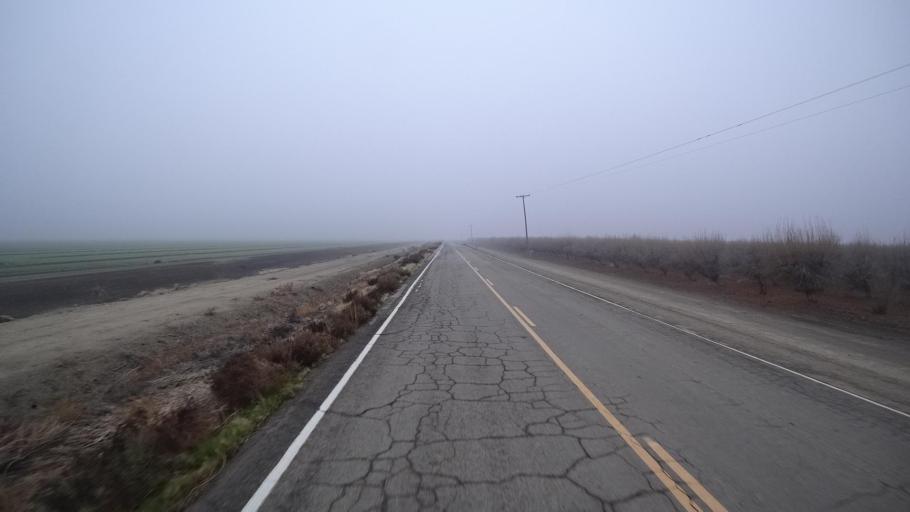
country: US
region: California
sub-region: Kern County
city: Lost Hills
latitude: 35.5693
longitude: -119.6183
